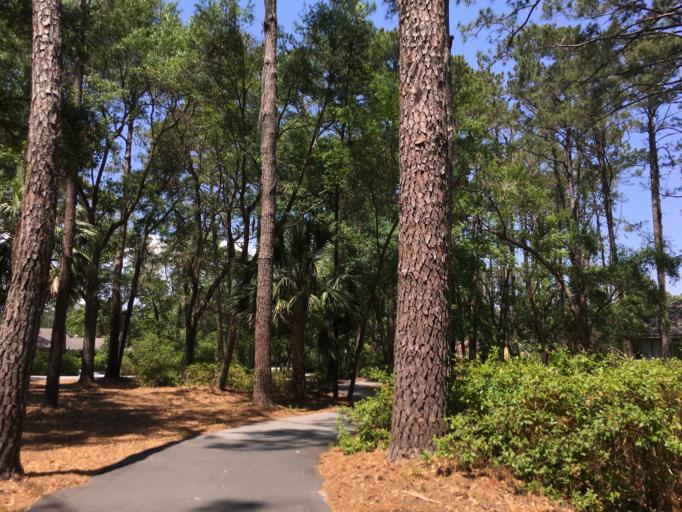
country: US
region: South Carolina
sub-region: Beaufort County
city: Hilton Head Island
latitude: 32.1227
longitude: -80.8107
